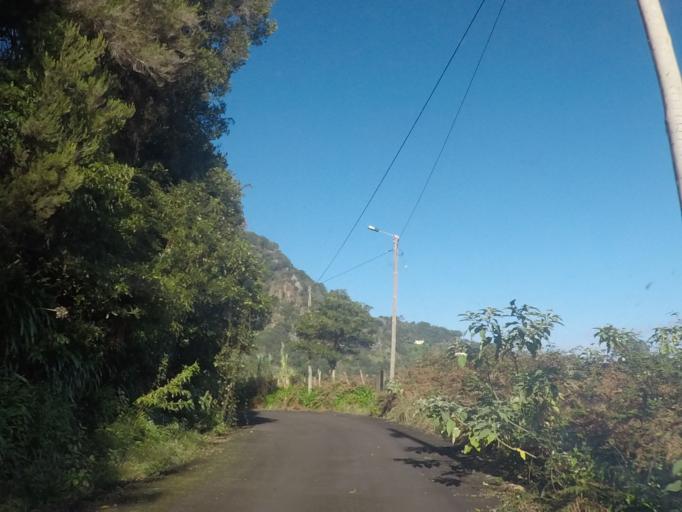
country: PT
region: Madeira
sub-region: Santana
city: Santana
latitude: 32.8171
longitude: -16.8960
